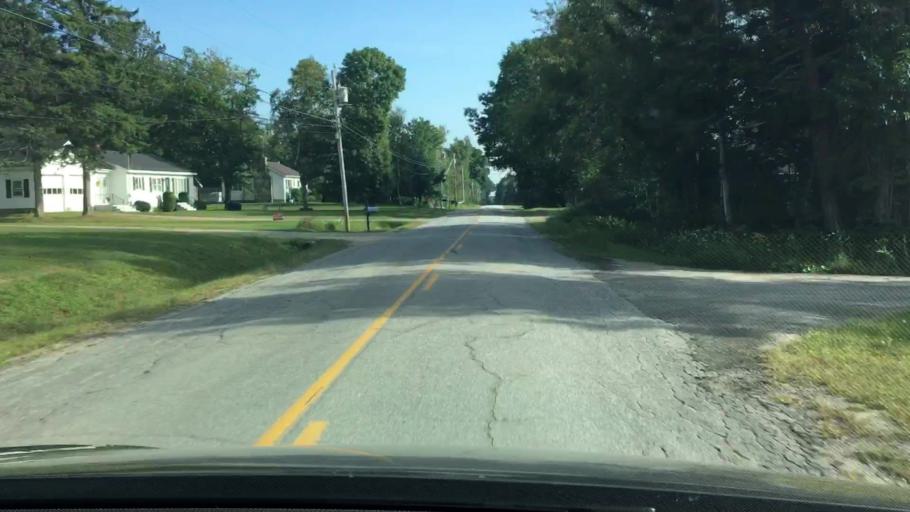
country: US
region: Maine
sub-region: Hancock County
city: Bucksport
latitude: 44.5454
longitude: -68.7968
